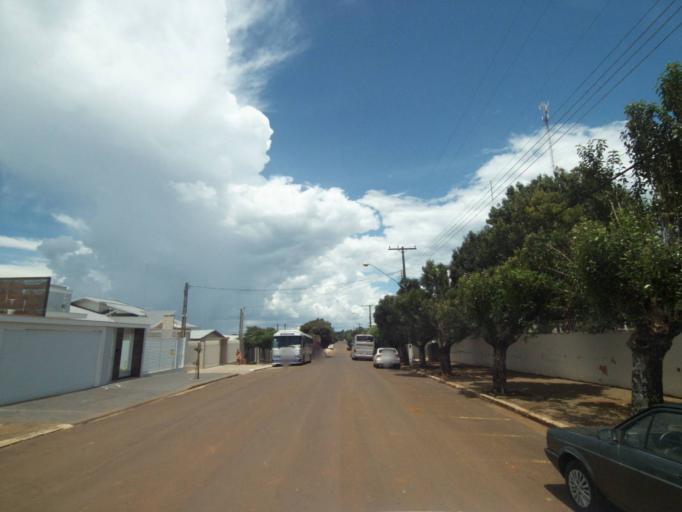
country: BR
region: Parana
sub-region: Guaraniacu
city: Guaraniacu
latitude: -25.0995
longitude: -52.8666
